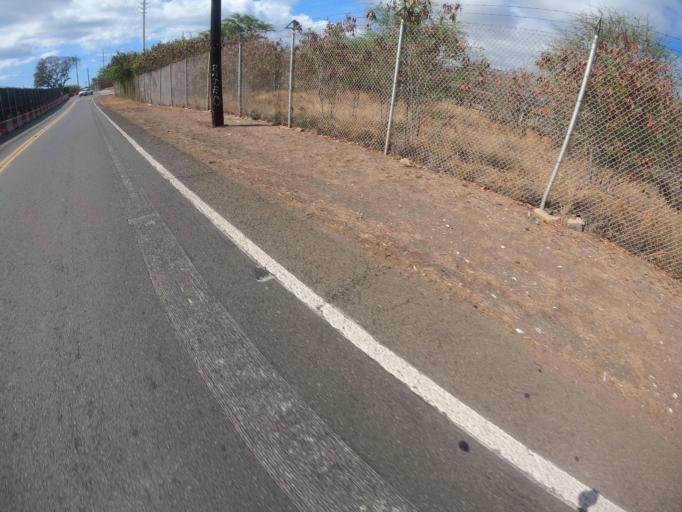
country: US
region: Hawaii
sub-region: Honolulu County
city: Makakilo City
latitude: 21.3252
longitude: -158.0858
